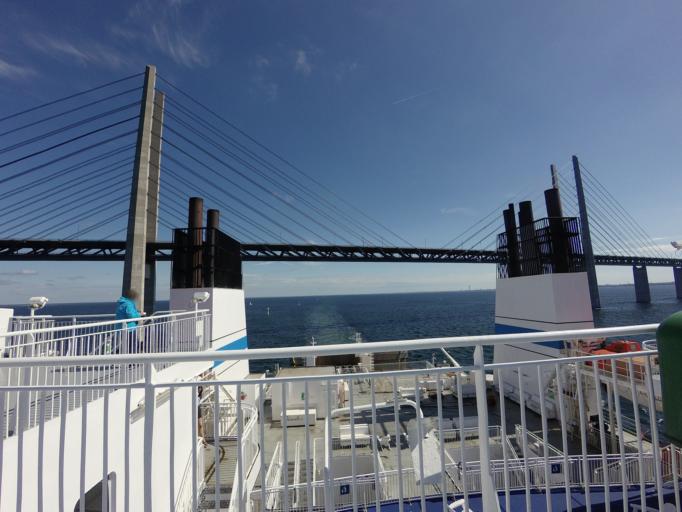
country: SE
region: Skane
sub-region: Malmo
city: Bunkeflostrand
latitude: 55.5737
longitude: 12.8227
